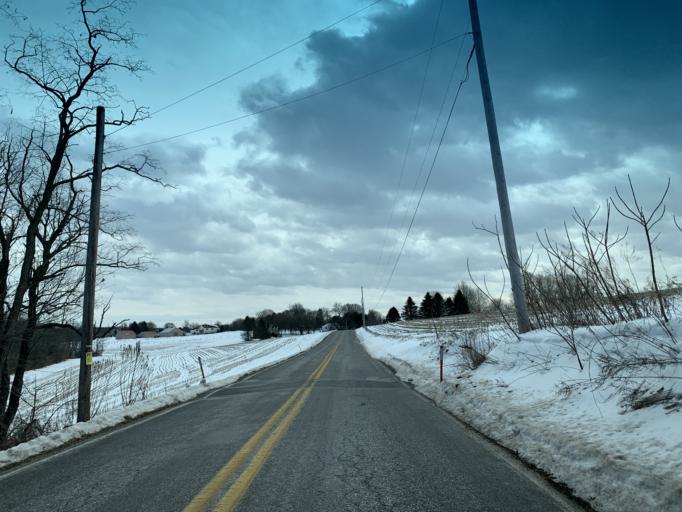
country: US
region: Pennsylvania
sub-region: York County
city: Shrewsbury
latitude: 39.7879
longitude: -76.6462
